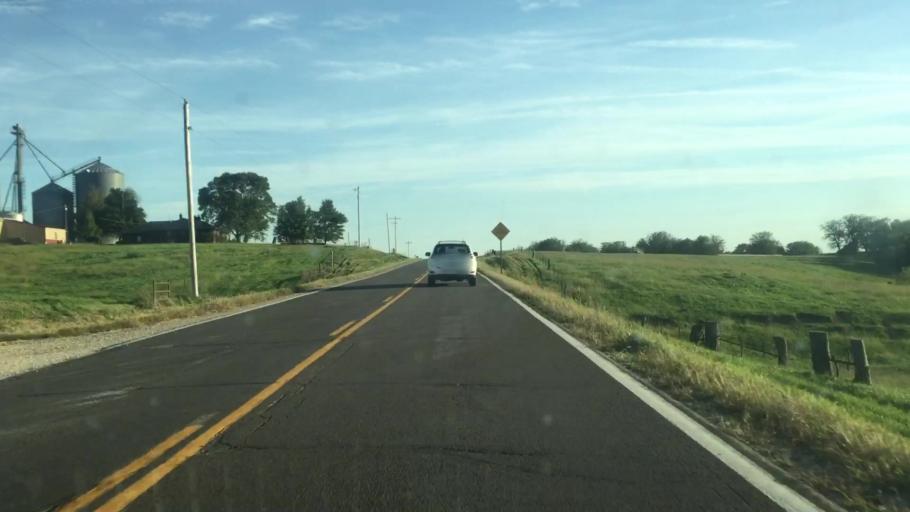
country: US
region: Kansas
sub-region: Brown County
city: Horton
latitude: 39.5765
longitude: -95.5271
